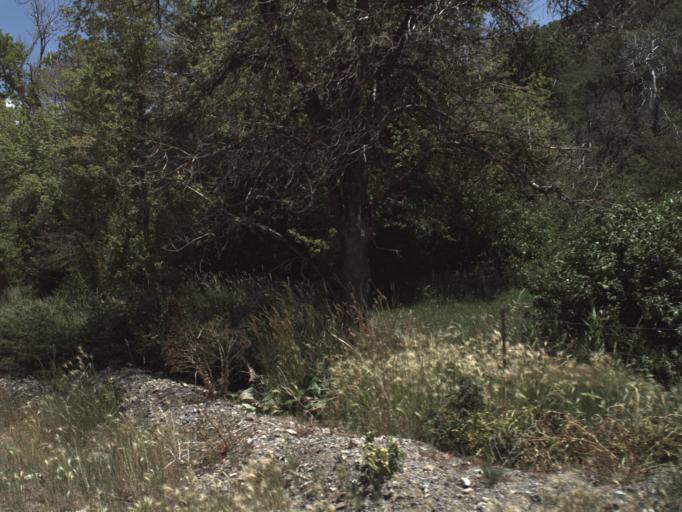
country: US
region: Utah
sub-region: Weber County
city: Wolf Creek
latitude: 41.2668
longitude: -111.6796
